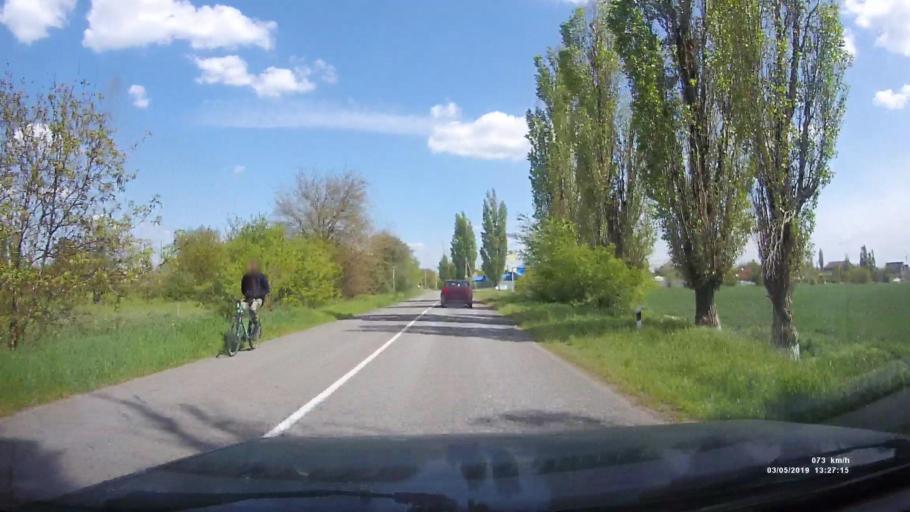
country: RU
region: Rostov
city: Semikarakorsk
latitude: 47.5751
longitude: 40.8312
